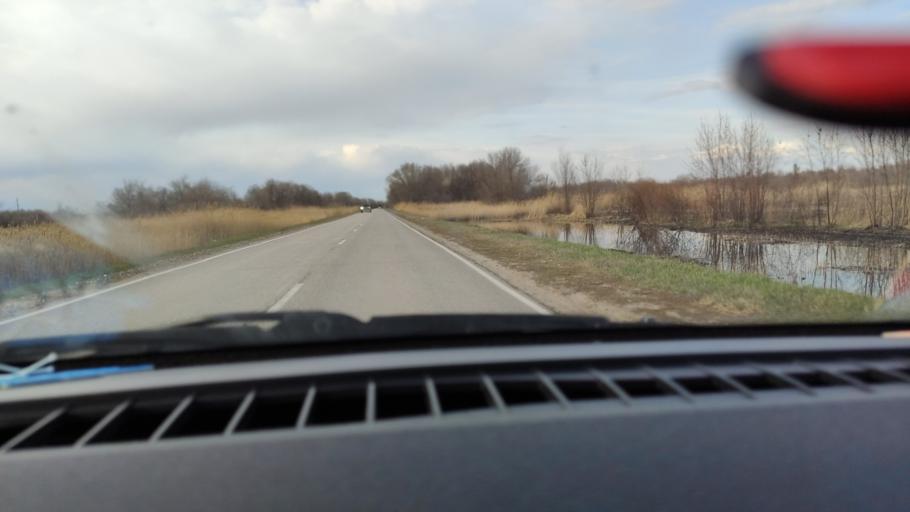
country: RU
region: Saratov
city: Privolzhskiy
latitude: 51.2700
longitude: 45.9470
